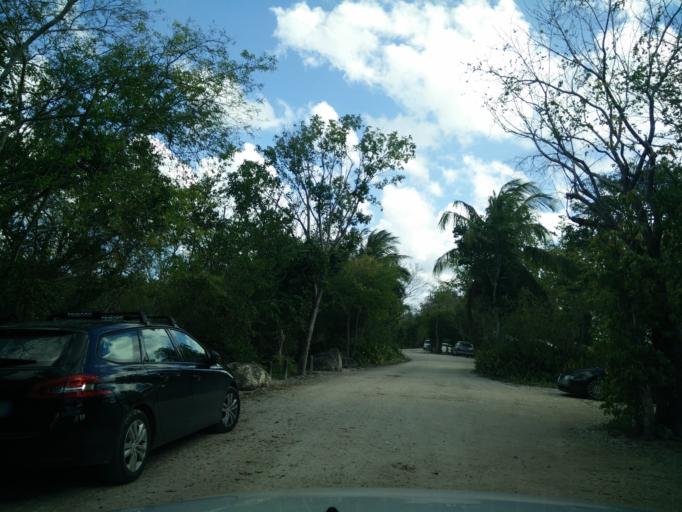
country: GP
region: Guadeloupe
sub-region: Guadeloupe
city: Port-Louis
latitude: 16.4372
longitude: -61.5372
